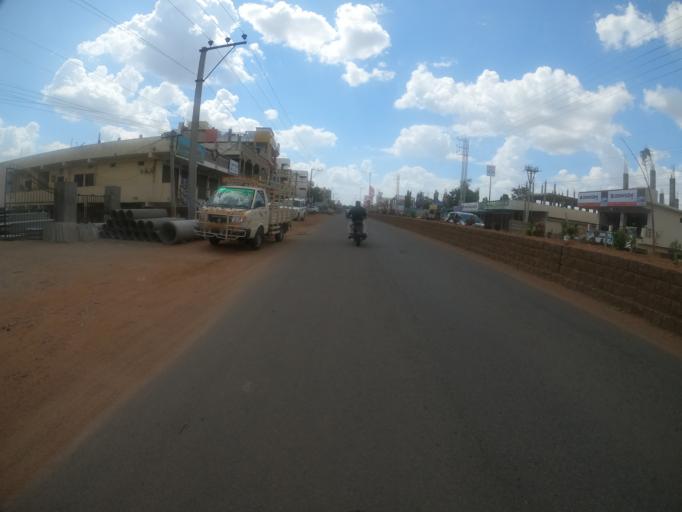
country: IN
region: Telangana
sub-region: Rangareddi
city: Sriramnagar
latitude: 17.3087
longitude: 78.1429
